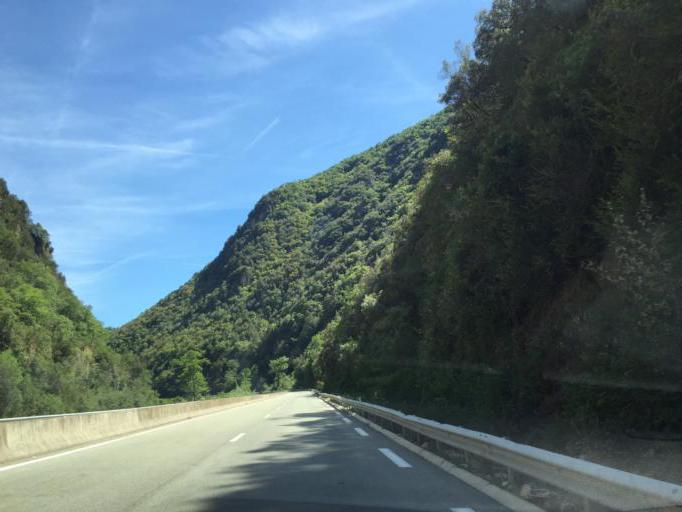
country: FR
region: Provence-Alpes-Cote d'Azur
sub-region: Departement des Alpes-Maritimes
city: Saint-Martin-Vesubie
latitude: 44.0132
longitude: 7.1315
